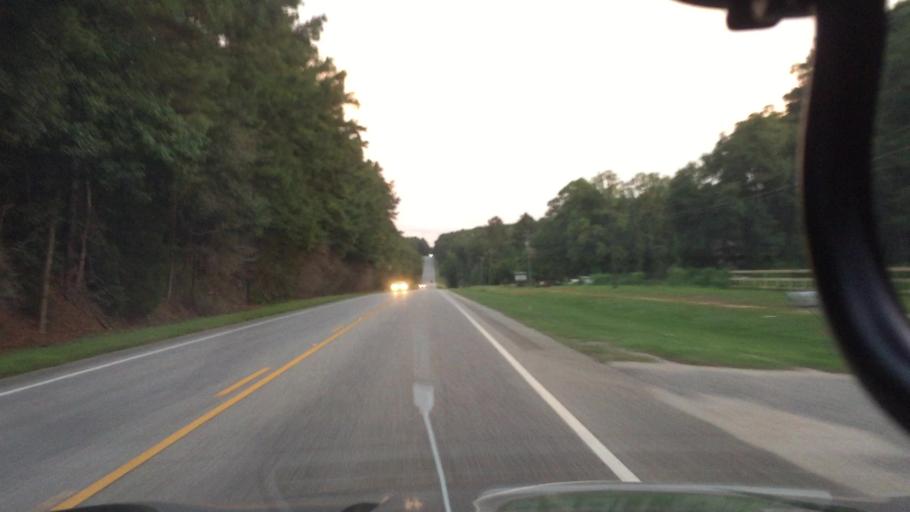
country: US
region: Alabama
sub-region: Coffee County
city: New Brockton
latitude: 31.3881
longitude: -85.8760
